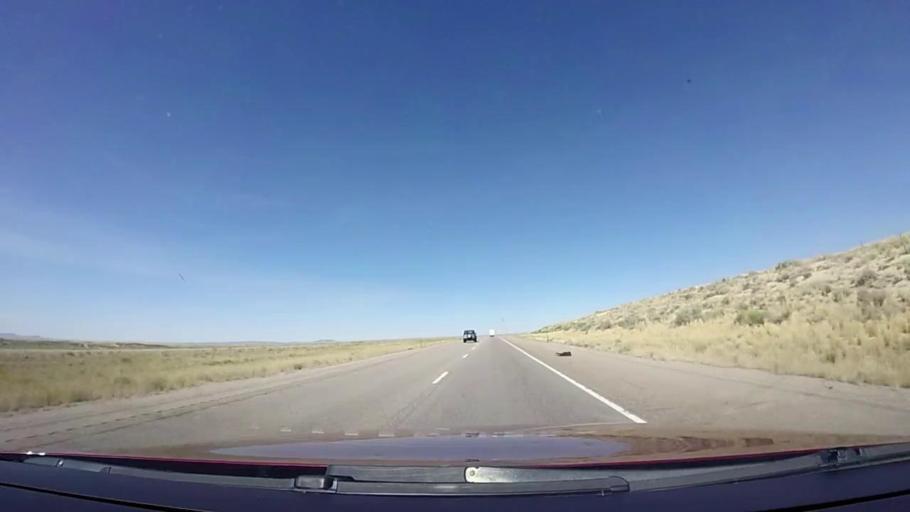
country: US
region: Wyoming
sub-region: Sweetwater County
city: Rock Springs
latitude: 41.6393
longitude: -108.4703
